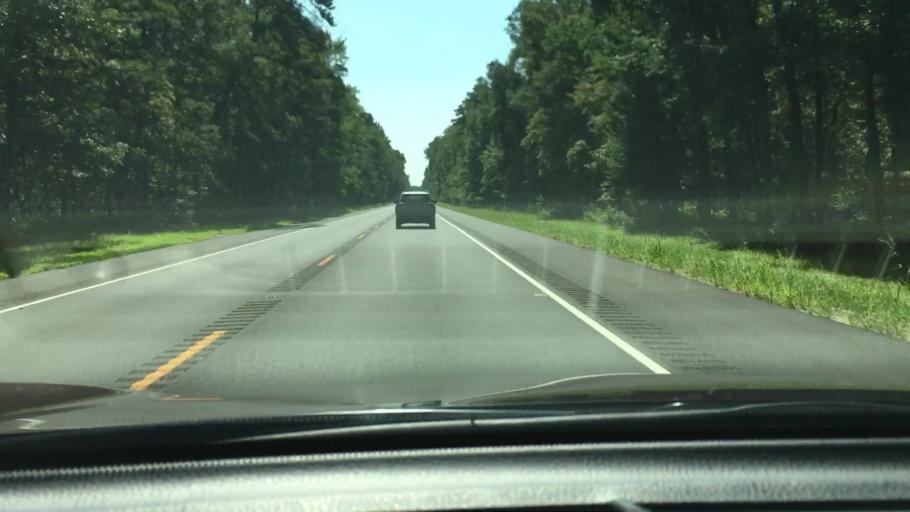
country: US
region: New Jersey
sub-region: Cape May County
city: Woodbine
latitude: 39.3349
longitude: -74.8830
